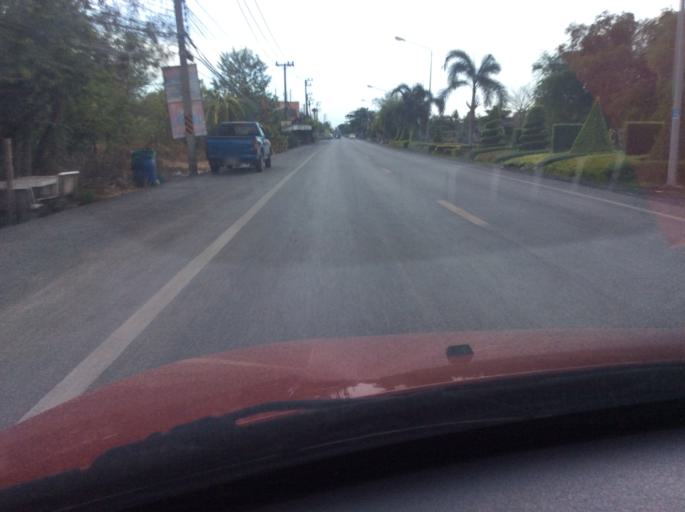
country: TH
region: Pathum Thani
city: Lam Luk Ka
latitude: 13.9529
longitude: 100.7272
